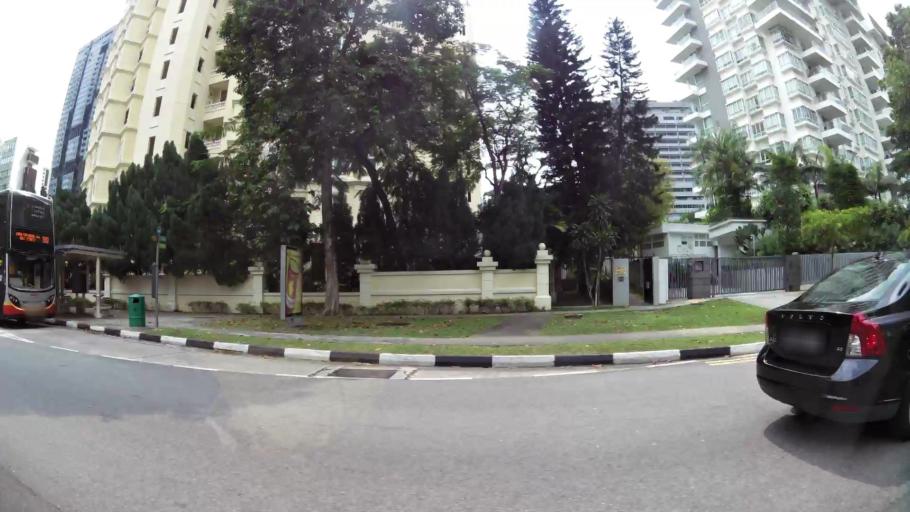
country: SG
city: Singapore
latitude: 1.3137
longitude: 103.8273
